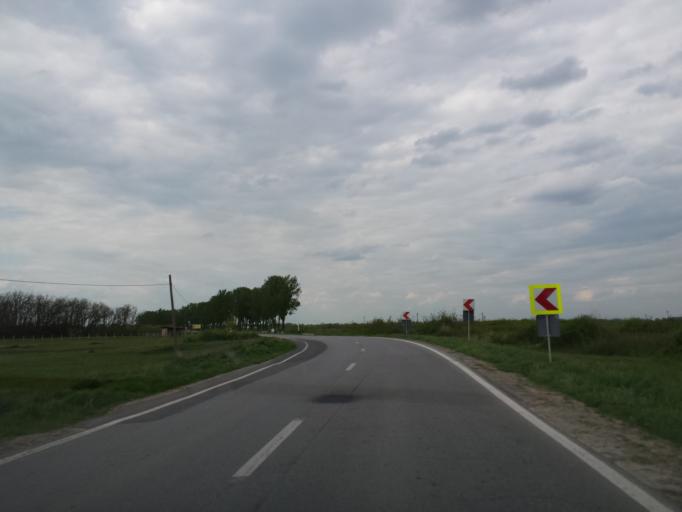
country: RO
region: Timis
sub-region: Comuna Cenad
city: Cenad
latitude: 46.1163
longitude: 20.5962
